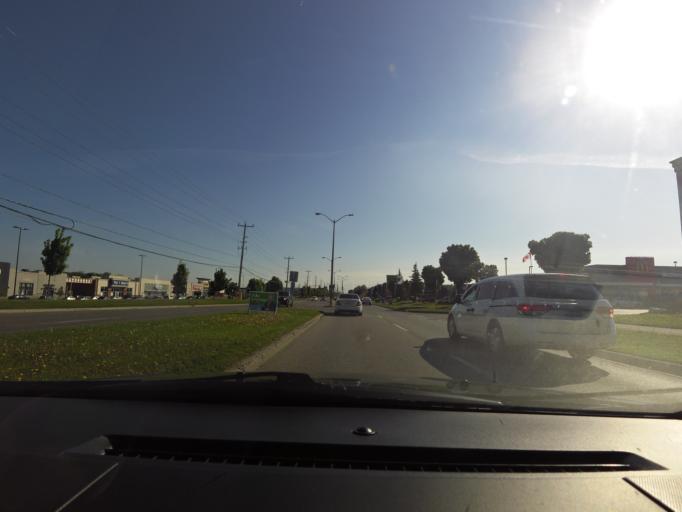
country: CA
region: Ontario
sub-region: Wellington County
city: Guelph
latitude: 43.5170
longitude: -80.2376
